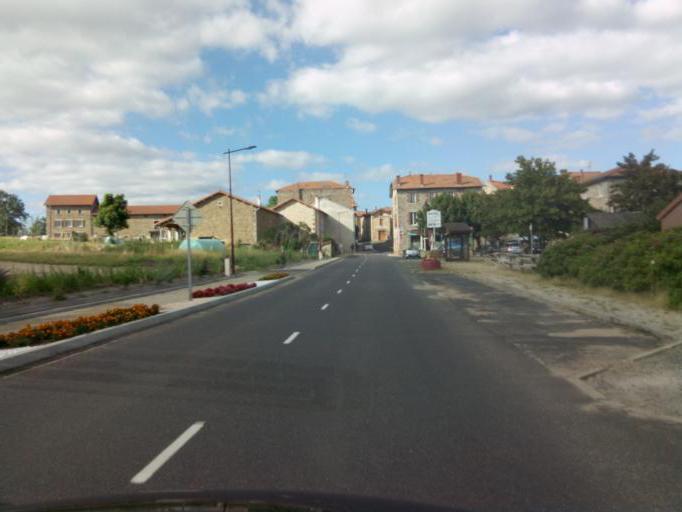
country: FR
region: Auvergne
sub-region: Departement de la Haute-Loire
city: Saint-Paulien
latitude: 45.2190
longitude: 3.8182
